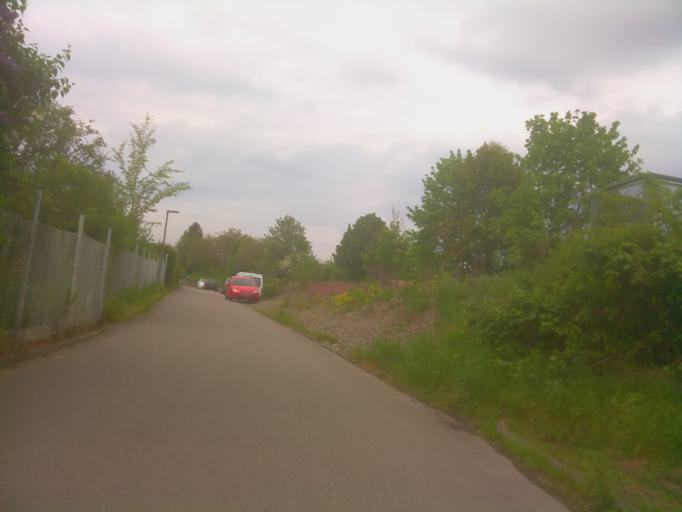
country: DE
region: Baden-Wuerttemberg
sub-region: Karlsruhe Region
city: Heidelberg
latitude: 49.3911
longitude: 8.6817
